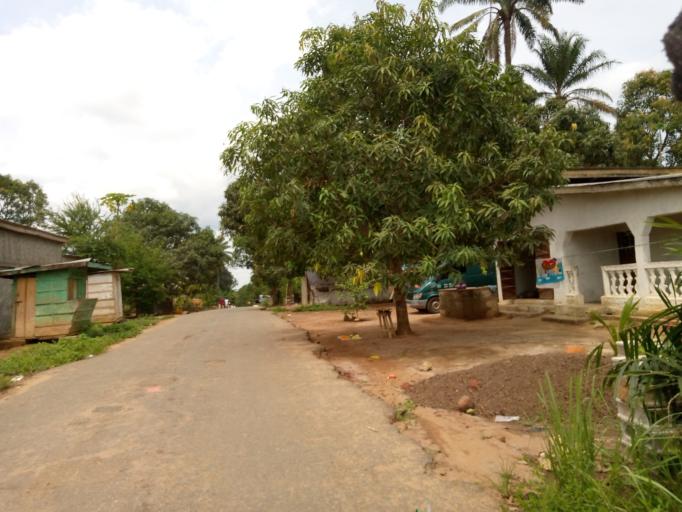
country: SL
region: Western Area
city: Waterloo
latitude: 8.3345
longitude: -13.0093
